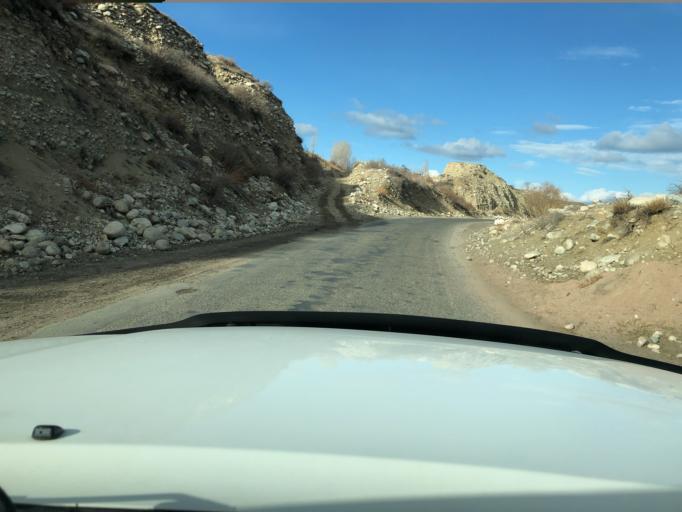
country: KG
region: Ysyk-Koel
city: Pokrovka
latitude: 42.1885
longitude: 77.6417
